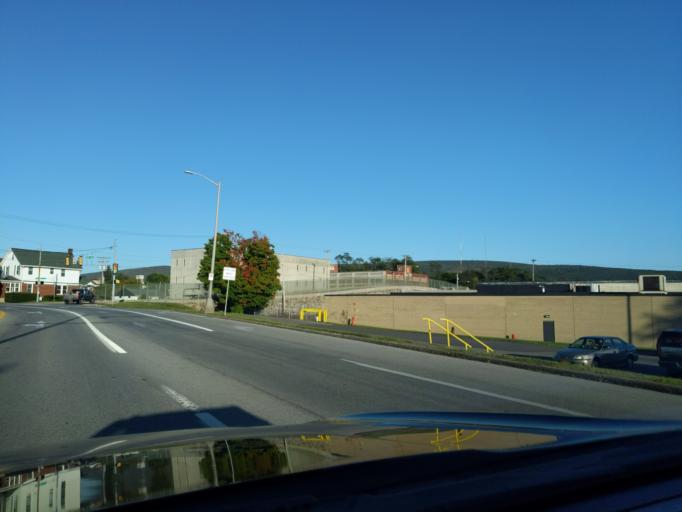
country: US
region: Pennsylvania
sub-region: Blair County
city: Altoona
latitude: 40.4988
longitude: -78.4145
